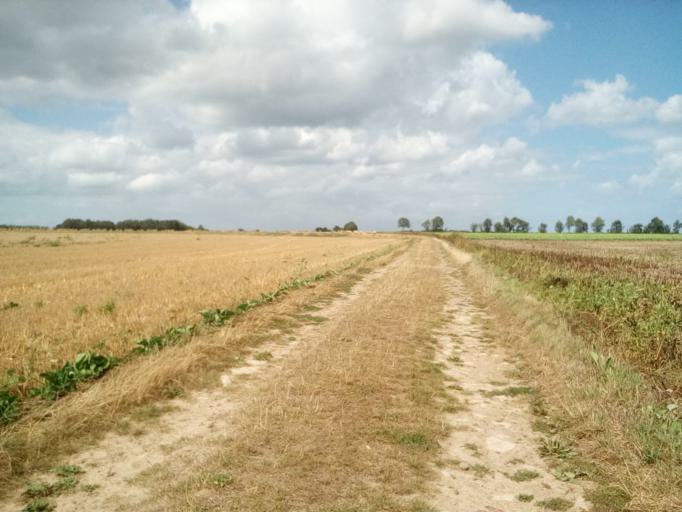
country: FR
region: Lower Normandy
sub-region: Departement du Calvados
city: Creully
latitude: 49.2929
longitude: -0.5698
